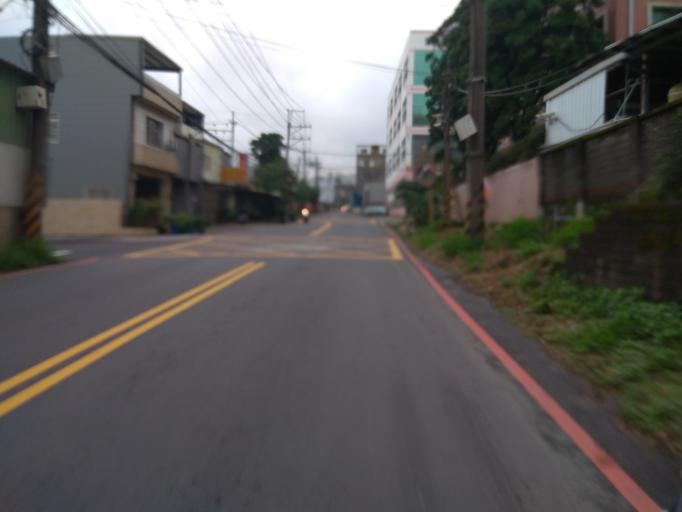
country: TW
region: Taiwan
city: Daxi
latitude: 24.9234
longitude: 121.1670
